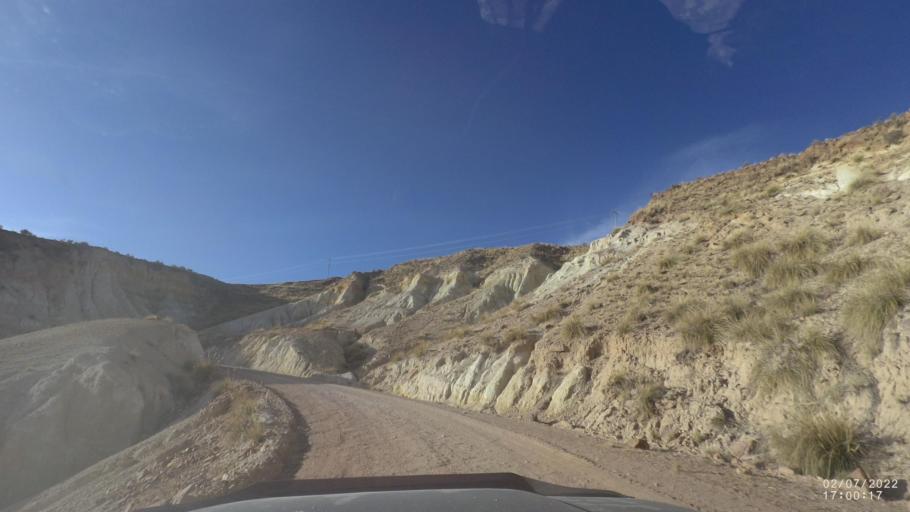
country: BO
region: Cochabamba
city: Irpa Irpa
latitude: -17.9380
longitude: -66.5535
